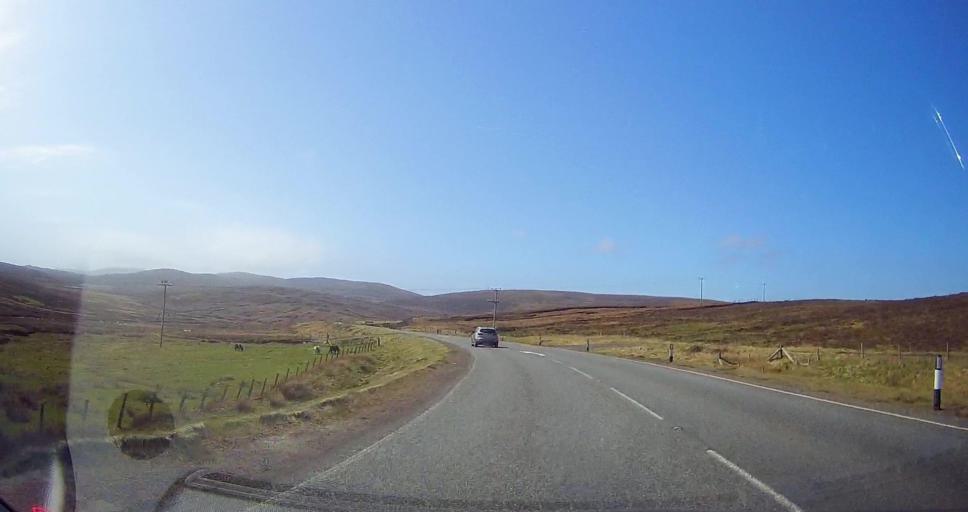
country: GB
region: Scotland
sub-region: Shetland Islands
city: Lerwick
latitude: 60.1397
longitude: -1.2238
